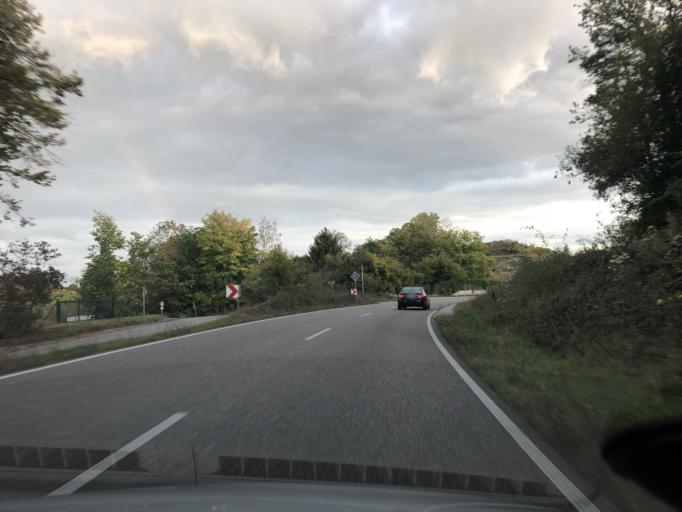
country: DE
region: Baden-Wuerttemberg
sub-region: Karlsruhe Region
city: Wimsheim
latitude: 48.8423
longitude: 8.8299
